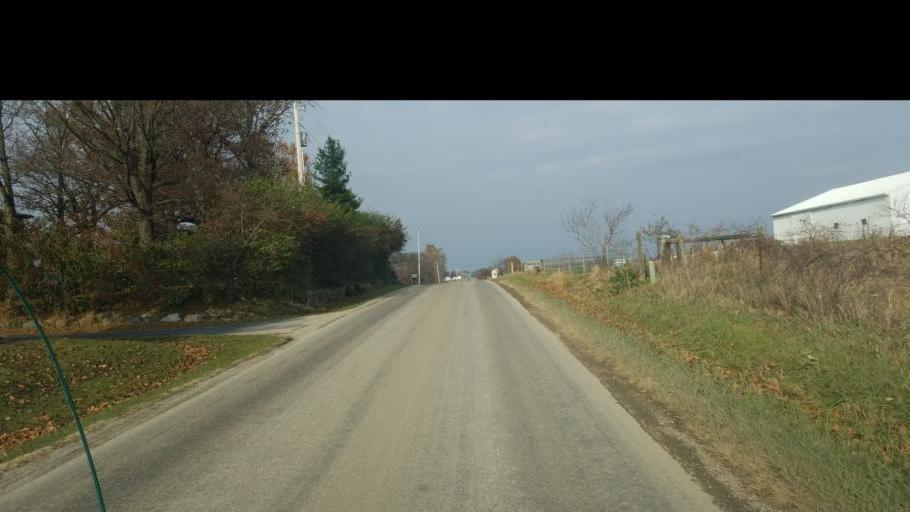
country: US
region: Indiana
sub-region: Adams County
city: Berne
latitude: 40.6253
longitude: -84.9356
